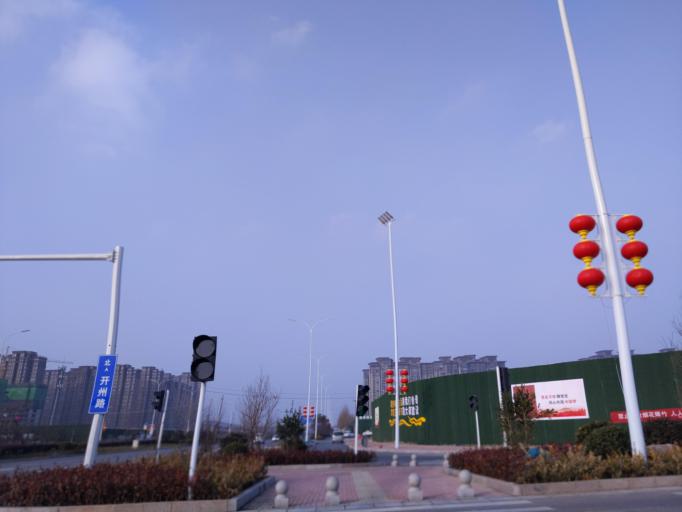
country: CN
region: Henan Sheng
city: Puyang
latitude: 35.8102
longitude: 115.0224
